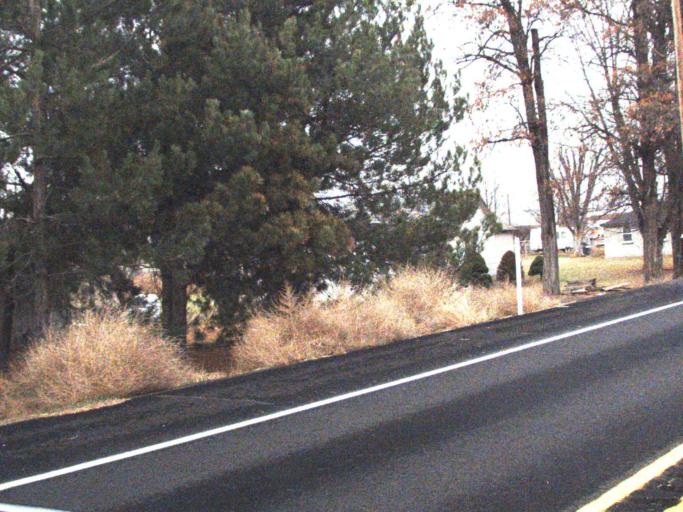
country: US
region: Washington
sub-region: Walla Walla County
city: Garrett
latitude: 46.0406
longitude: -118.6711
